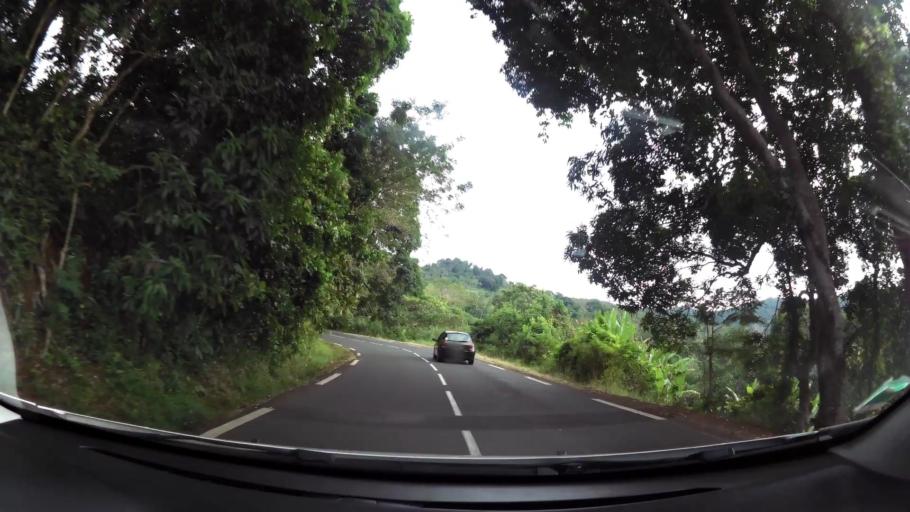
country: YT
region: Dembeni
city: Dembeni
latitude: -12.8399
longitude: 45.1659
